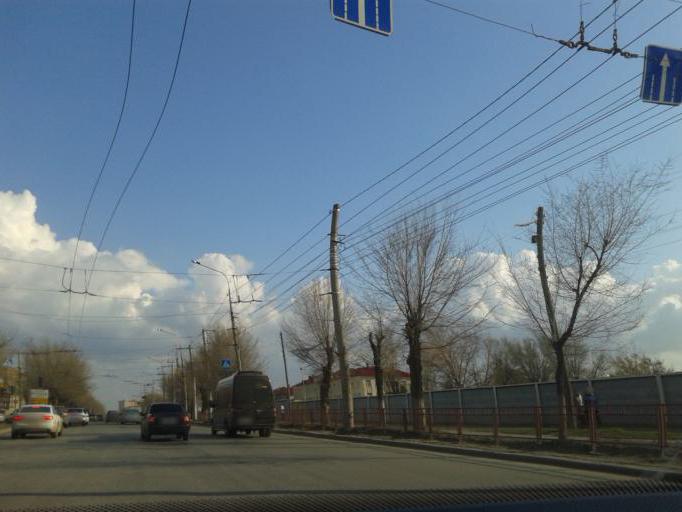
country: RU
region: Volgograd
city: Volgograd
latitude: 48.7351
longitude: 44.4945
